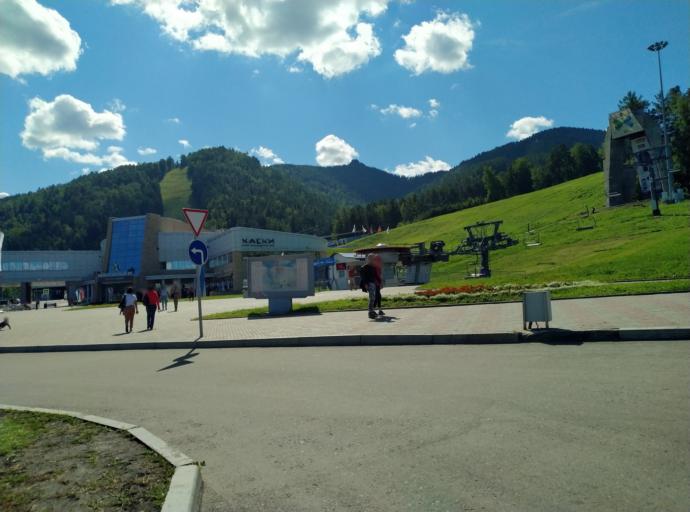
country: RU
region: Krasnoyarskiy
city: Krasnoyarsk
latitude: 55.9624
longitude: 92.7940
